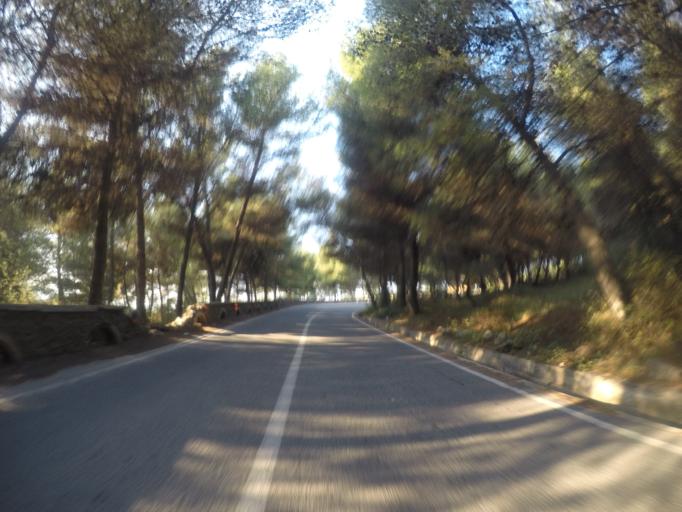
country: AL
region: Durres
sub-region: Rrethi i Krujes
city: Kruje
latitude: 41.4915
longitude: 19.7670
